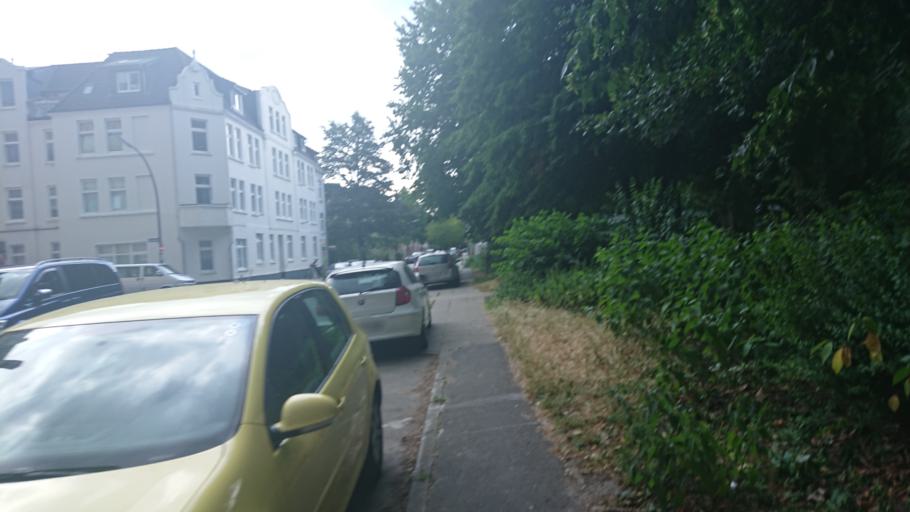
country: DE
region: Hamburg
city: Harburg
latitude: 53.4566
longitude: 9.9754
